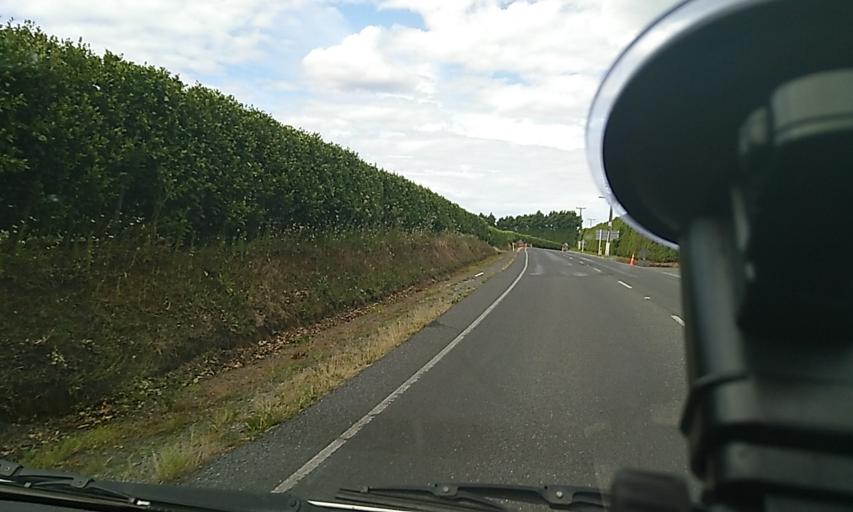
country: NZ
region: Bay of Plenty
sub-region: Western Bay of Plenty District
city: Waihi Beach
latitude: -37.4510
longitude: 175.9485
